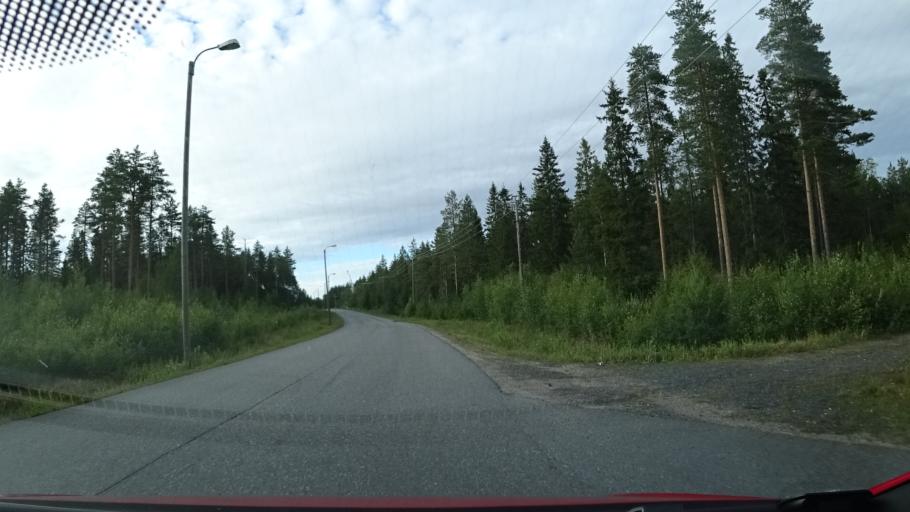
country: FI
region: Northern Ostrobothnia
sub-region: Oulu
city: Haukipudas
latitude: 65.1974
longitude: 25.4135
